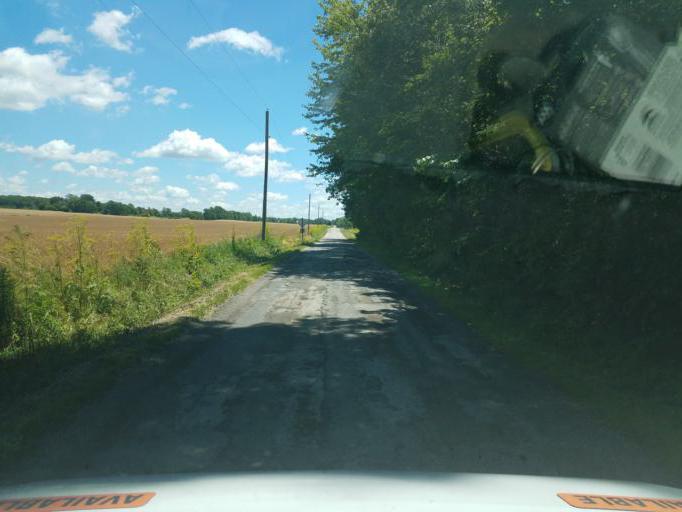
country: US
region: Ohio
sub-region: Crawford County
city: Galion
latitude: 40.7125
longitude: -82.8565
